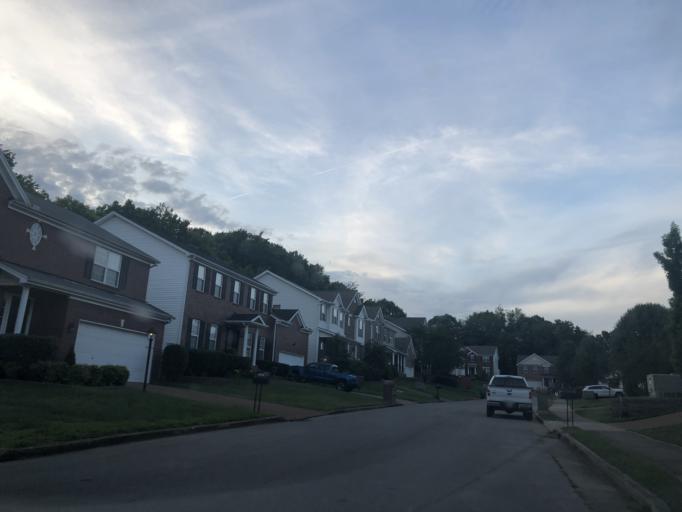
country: US
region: Tennessee
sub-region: Cheatham County
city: Pegram
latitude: 36.0476
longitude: -86.9582
